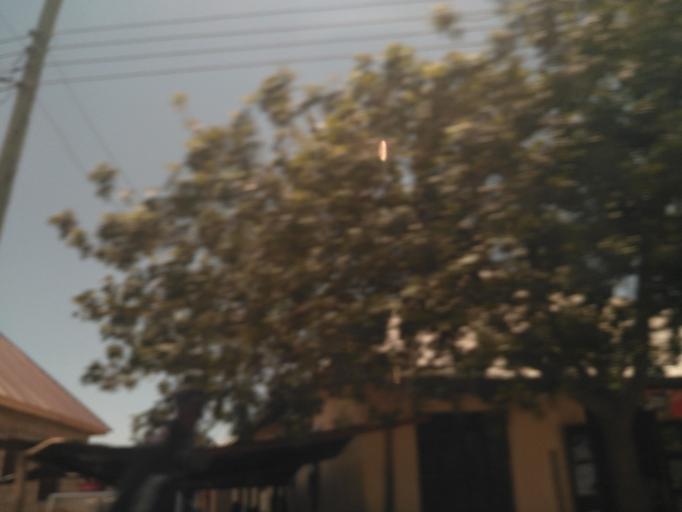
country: TZ
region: Dodoma
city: Dodoma
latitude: -6.1482
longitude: 35.7391
